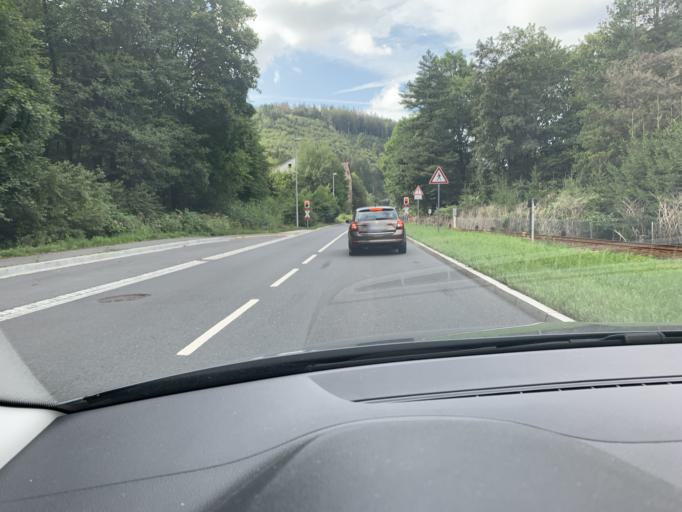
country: DE
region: Thuringia
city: Sonneberg
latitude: 50.3674
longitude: 11.2049
